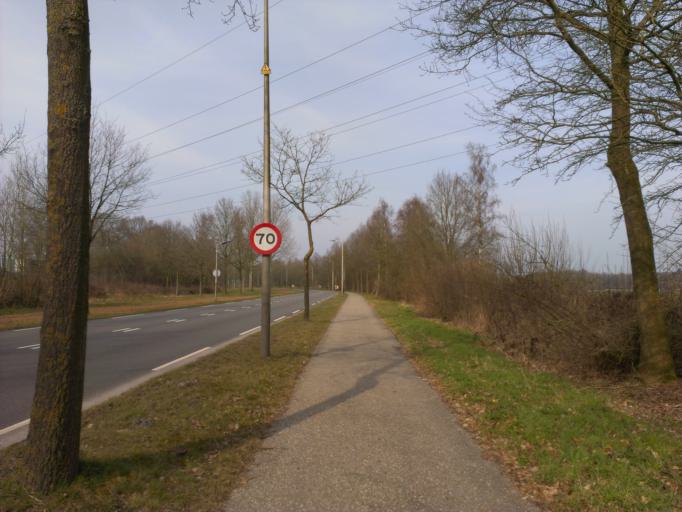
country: NL
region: Drenthe
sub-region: Gemeente Hoogeveen
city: Hoogeveen
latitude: 52.7362
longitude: 6.5026
